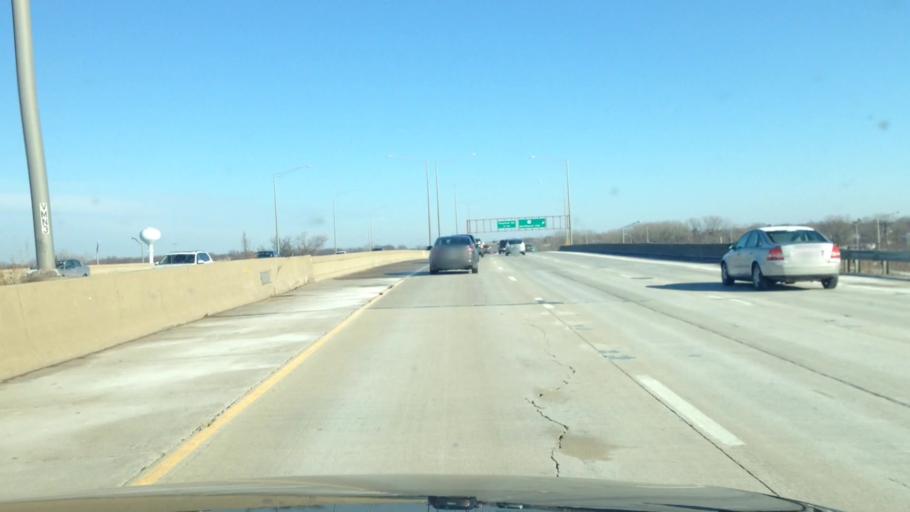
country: US
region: Illinois
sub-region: Cook County
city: Rolling Meadows
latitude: 42.0996
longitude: -88.0196
